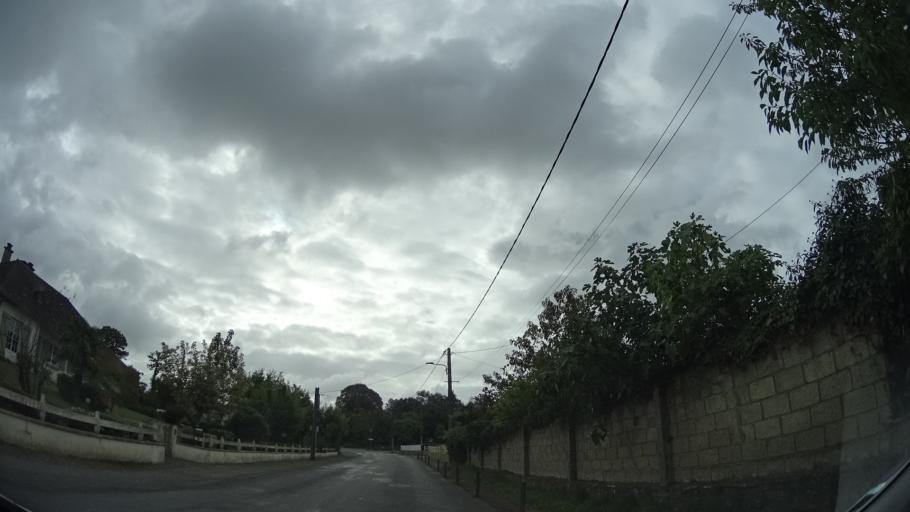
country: FR
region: Brittany
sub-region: Departement d'Ille-et-Vilaine
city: Montreuil-sur-Ille
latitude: 48.3051
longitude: -1.6657
